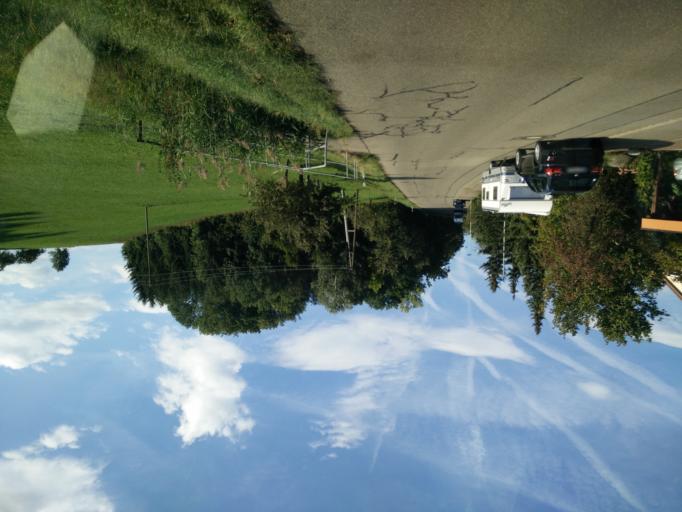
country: DE
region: Baden-Wuerttemberg
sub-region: Tuebingen Region
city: Kirchentellinsfurt
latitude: 48.5271
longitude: 9.1561
